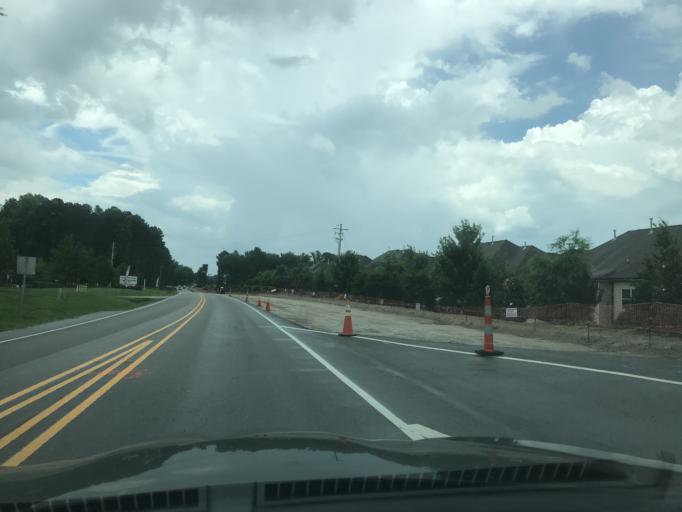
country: US
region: North Carolina
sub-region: Wake County
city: Knightdale
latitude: 35.8408
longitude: -78.5063
